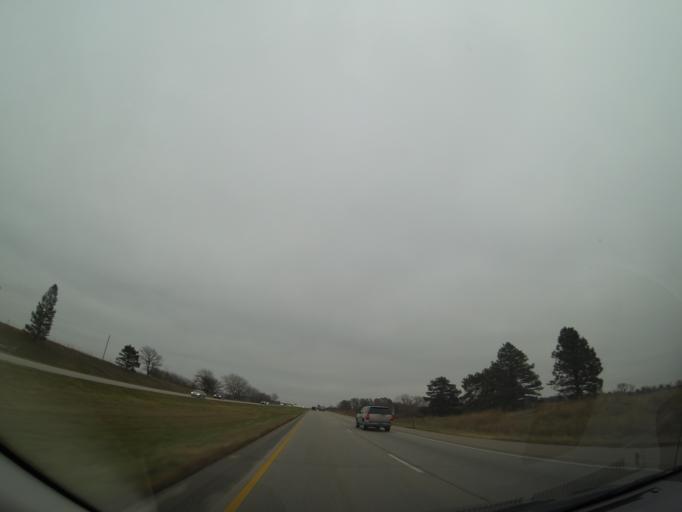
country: US
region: Nebraska
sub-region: Seward County
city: Milford
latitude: 40.8209
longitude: -97.0054
